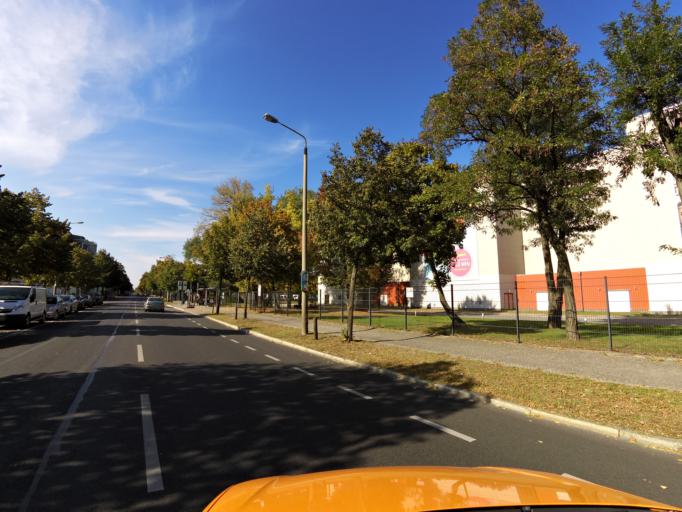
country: DE
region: Berlin
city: Wannsee
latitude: 52.3840
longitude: 13.1179
